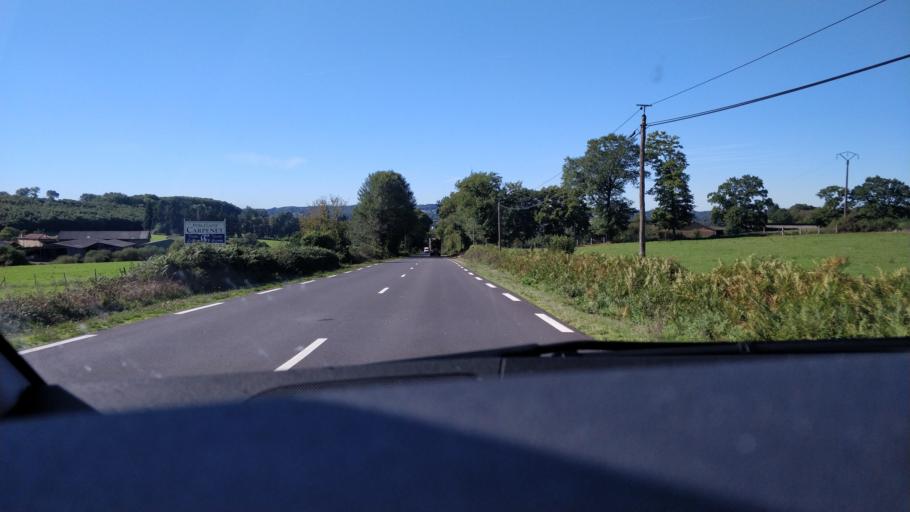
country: FR
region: Limousin
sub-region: Departement de la Haute-Vienne
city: Saint-Leonard-de-Noblat
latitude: 45.8574
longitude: 1.5095
